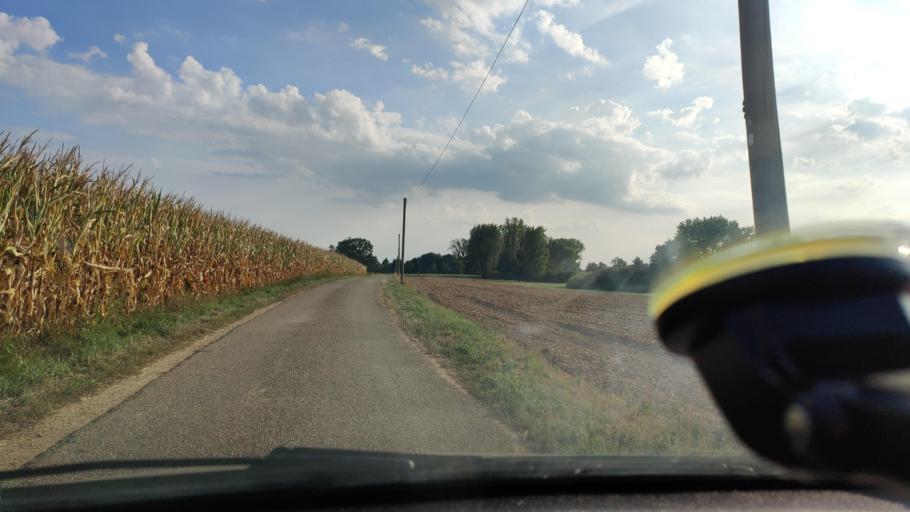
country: DE
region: North Rhine-Westphalia
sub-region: Regierungsbezirk Dusseldorf
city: Sonsbeck
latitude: 51.5658
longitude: 6.3668
